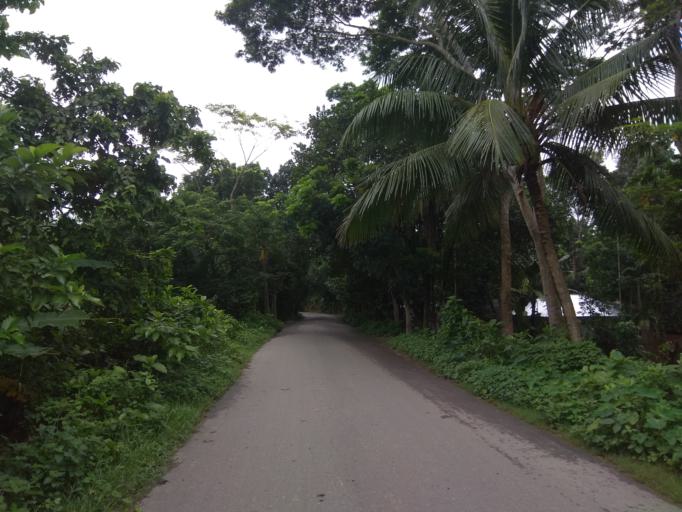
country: BD
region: Dhaka
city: Dohar
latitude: 23.4328
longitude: 90.0729
